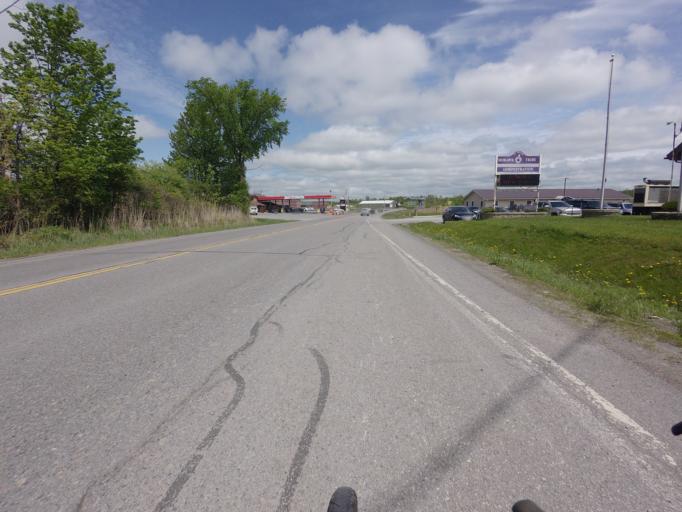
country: CA
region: Ontario
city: Cornwall
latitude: 44.9786
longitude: -74.6850
